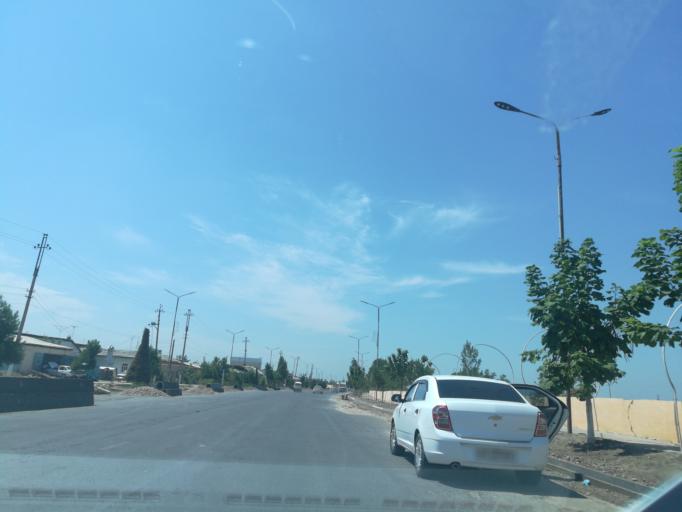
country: UZ
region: Namangan
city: Uchqurghon Shahri
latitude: 41.0733
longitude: 72.0349
